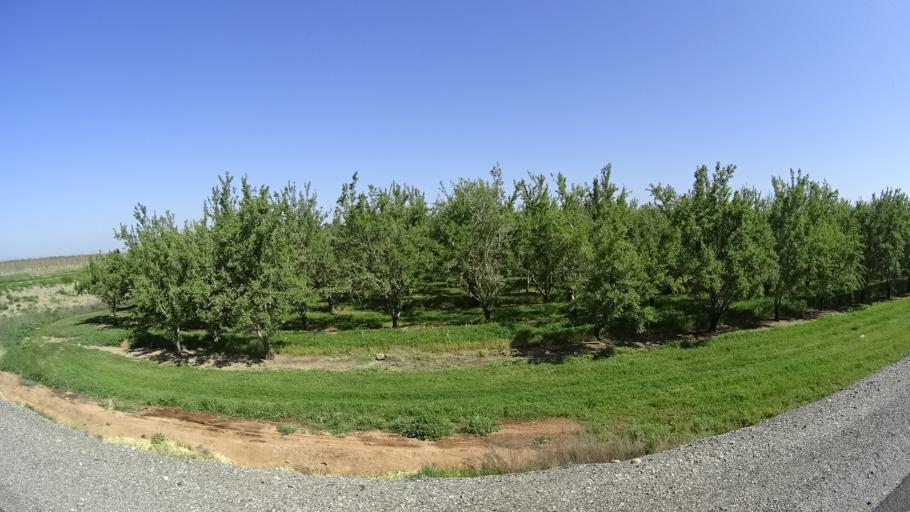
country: US
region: California
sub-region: Glenn County
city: Hamilton City
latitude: 39.6596
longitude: -122.0263
